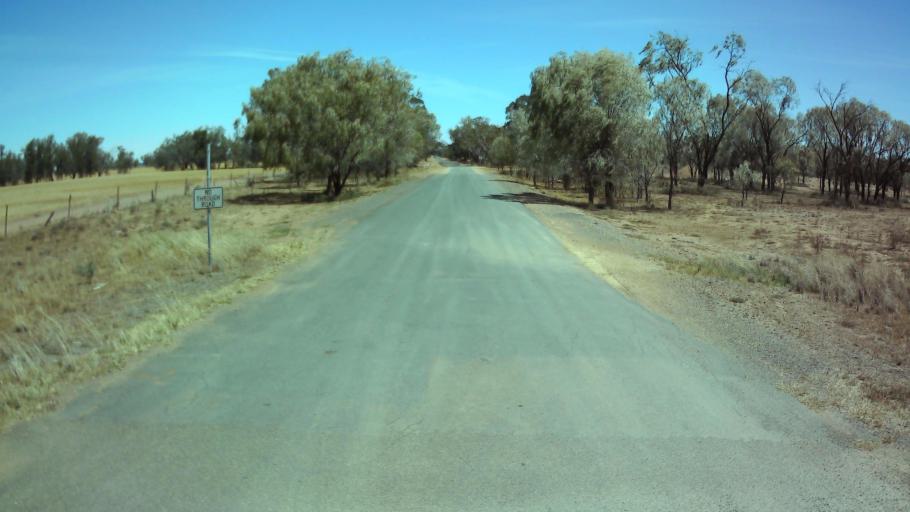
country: AU
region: New South Wales
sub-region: Weddin
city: Grenfell
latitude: -33.8403
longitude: 147.6975
